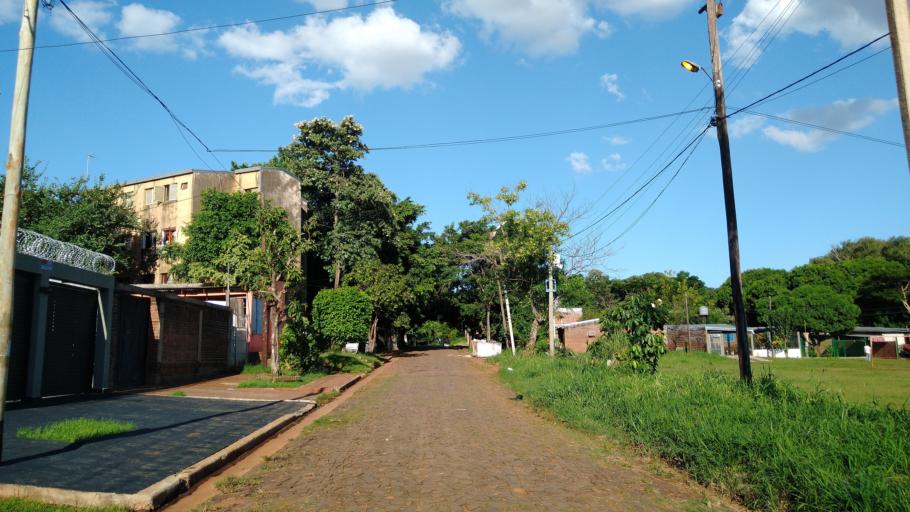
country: AR
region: Misiones
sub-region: Departamento de Capital
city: Posadas
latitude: -27.3588
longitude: -55.9320
